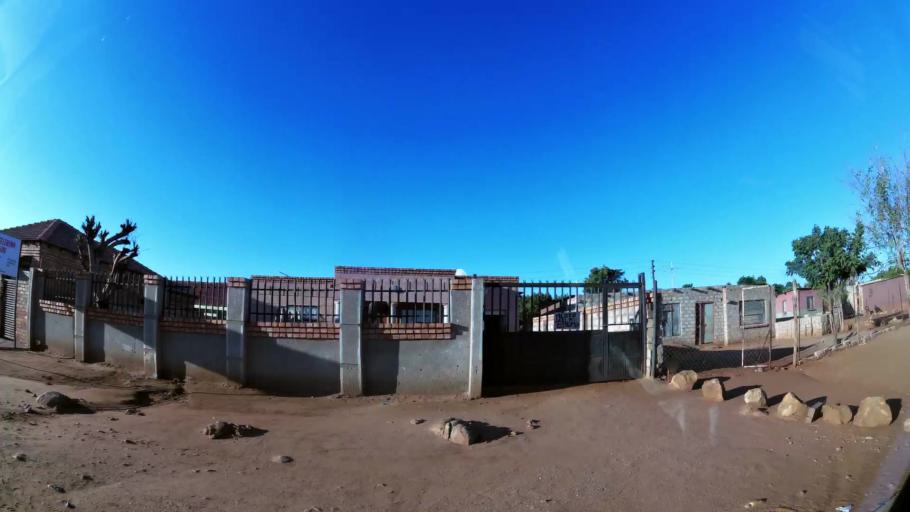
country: ZA
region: Limpopo
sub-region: Waterberg District Municipality
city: Mokopane
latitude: -24.1474
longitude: 28.9977
